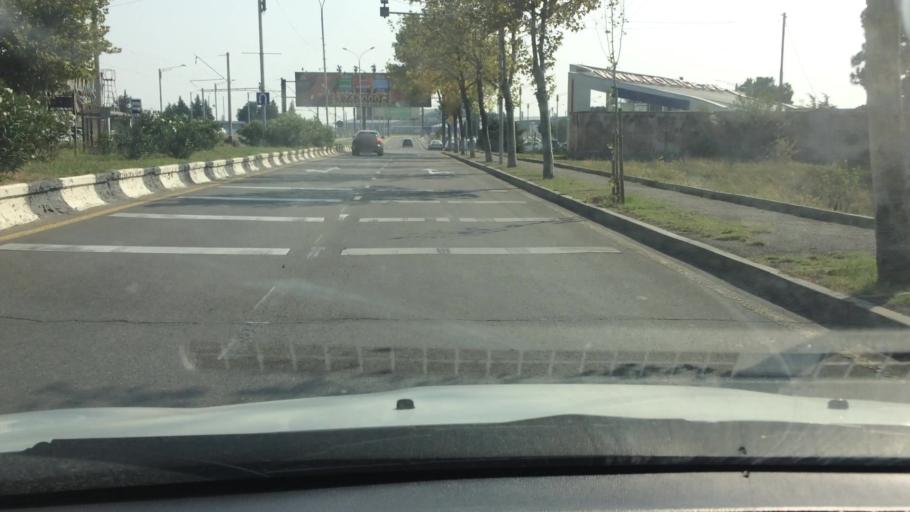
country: GE
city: Didi Lilo
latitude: 41.6751
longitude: 44.9612
